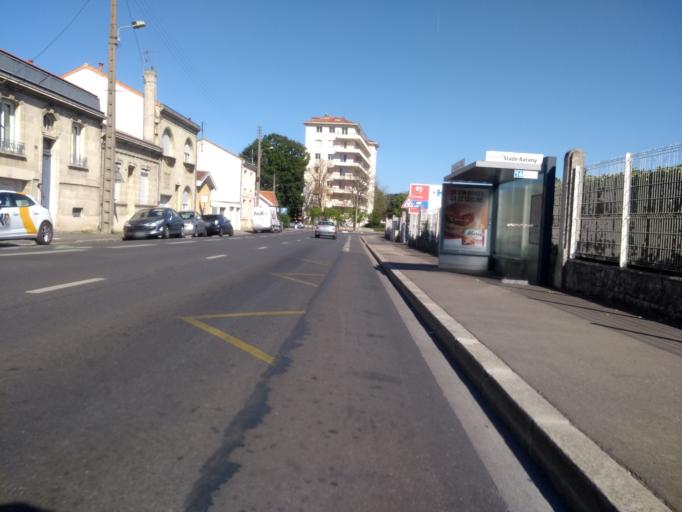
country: FR
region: Aquitaine
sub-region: Departement de la Gironde
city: Bordeaux
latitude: 44.8423
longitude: -0.6074
